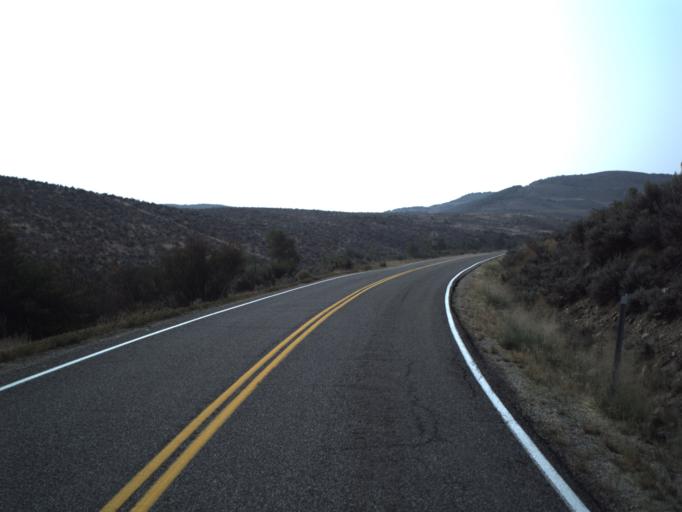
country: US
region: Utah
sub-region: Summit County
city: Coalville
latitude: 40.9782
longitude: -111.5375
